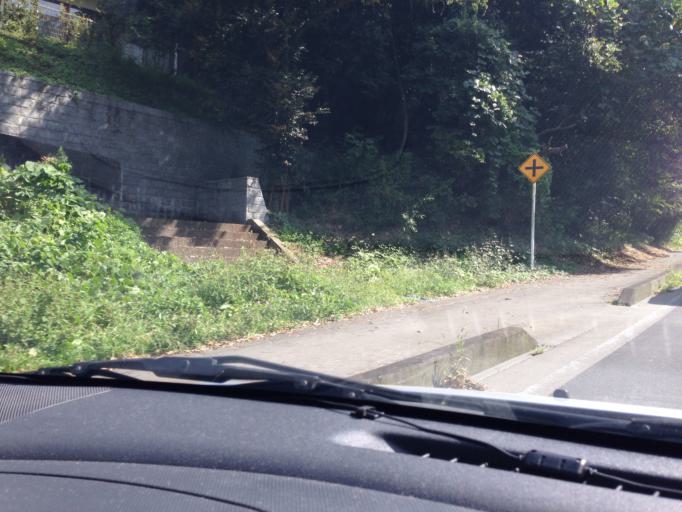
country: JP
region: Ibaraki
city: Mito-shi
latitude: 36.4112
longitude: 140.4266
